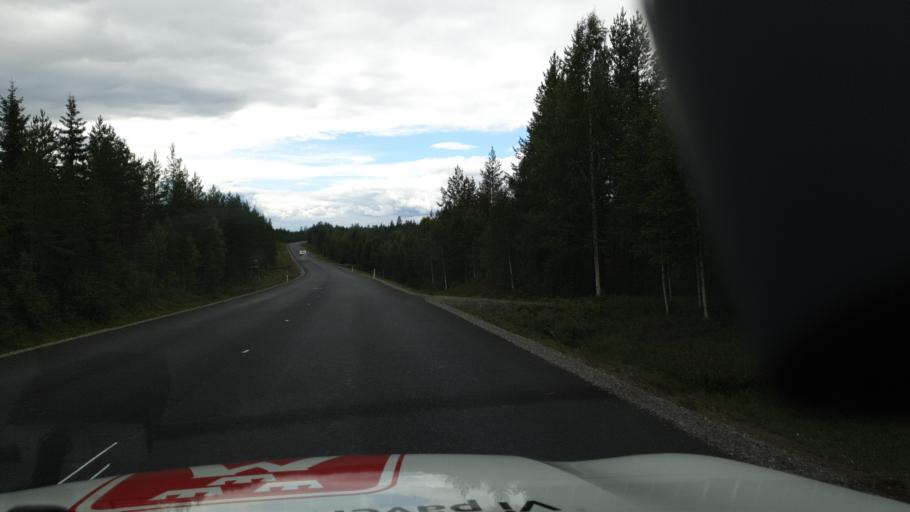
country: SE
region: Vaesterbotten
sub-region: Skelleftea Kommun
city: Langsele
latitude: 64.8873
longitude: 20.2471
